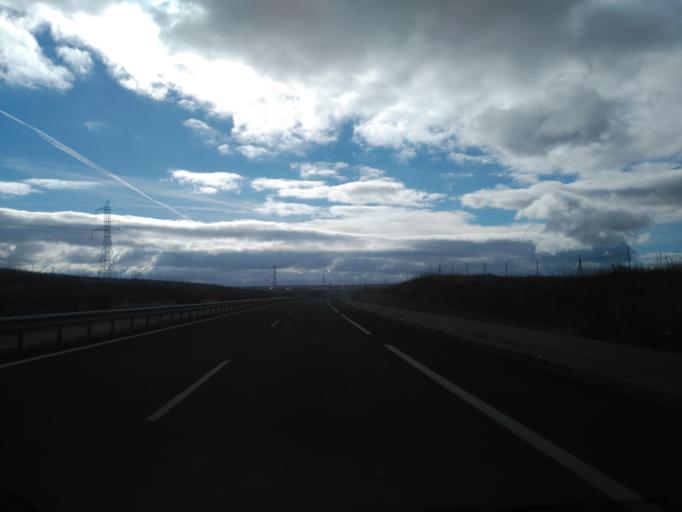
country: ES
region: Castille and Leon
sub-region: Provincia de Palencia
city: Abia de las Torres
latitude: 42.3857
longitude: -4.3859
